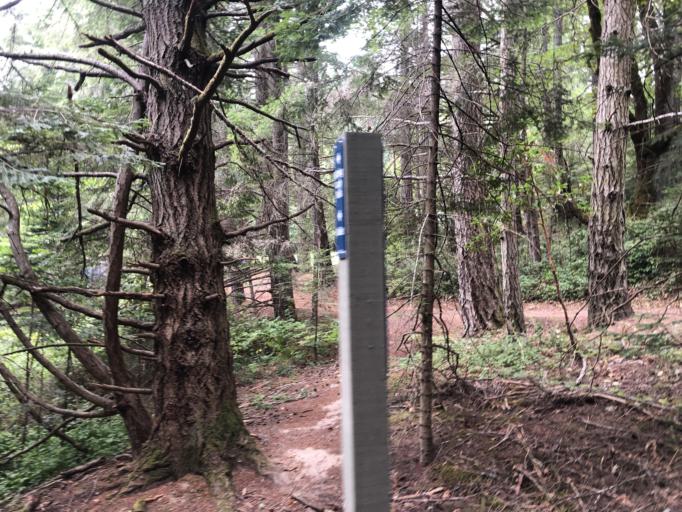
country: CA
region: British Columbia
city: Metchosin
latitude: 48.3888
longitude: -123.5203
